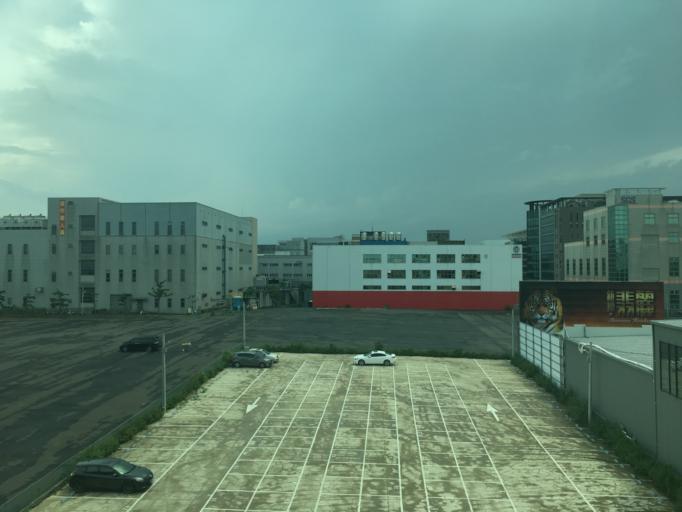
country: TW
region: Taiwan
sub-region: Taoyuan
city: Taoyuan
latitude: 25.0515
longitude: 121.3798
